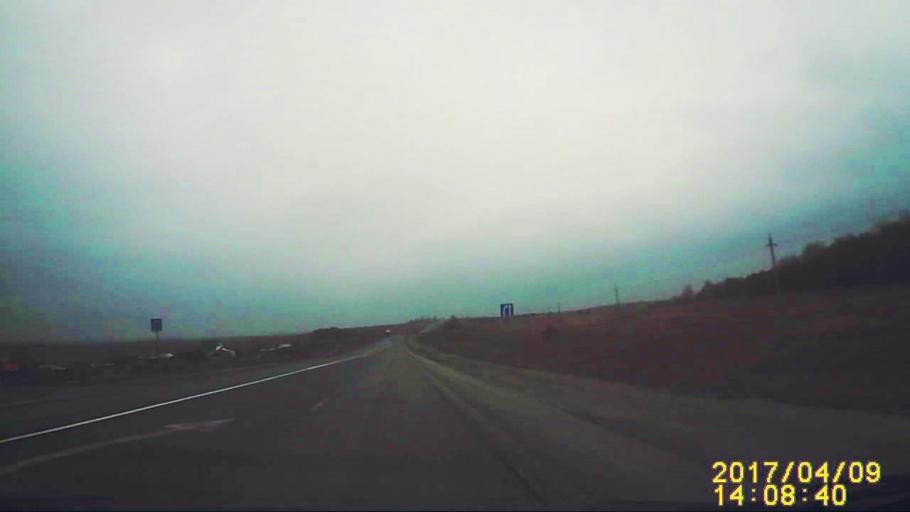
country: RU
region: Ulyanovsk
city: Silikatnyy
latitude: 54.0219
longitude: 48.2149
